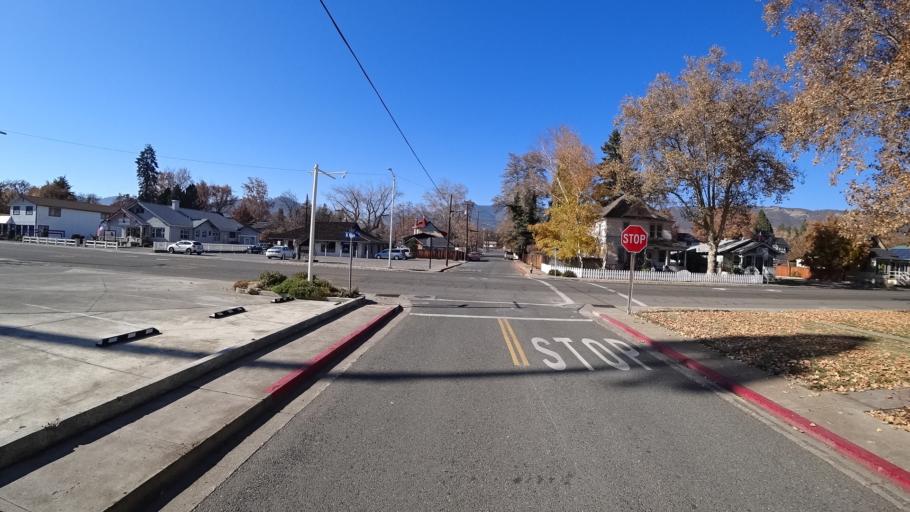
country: US
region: California
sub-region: Siskiyou County
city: Yreka
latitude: 41.7350
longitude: -122.6344
